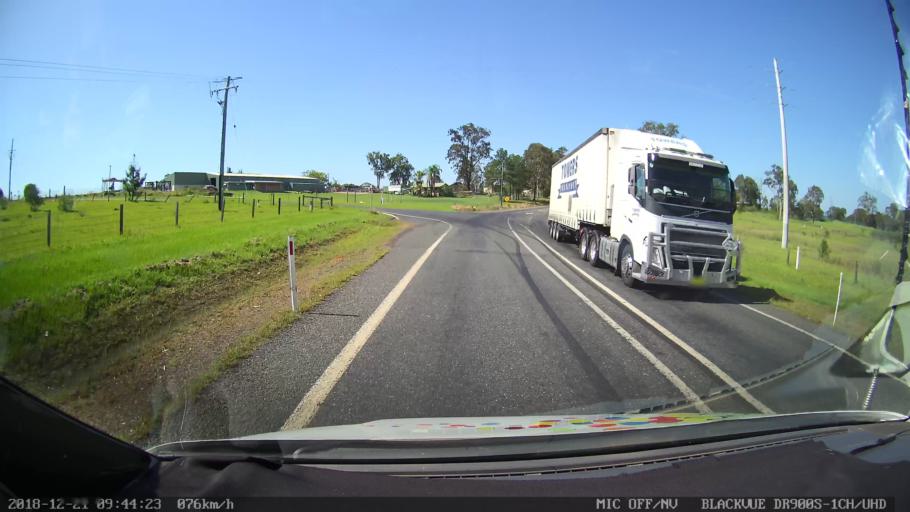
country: AU
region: New South Wales
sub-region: Clarence Valley
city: Grafton
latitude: -29.6175
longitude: 152.9338
